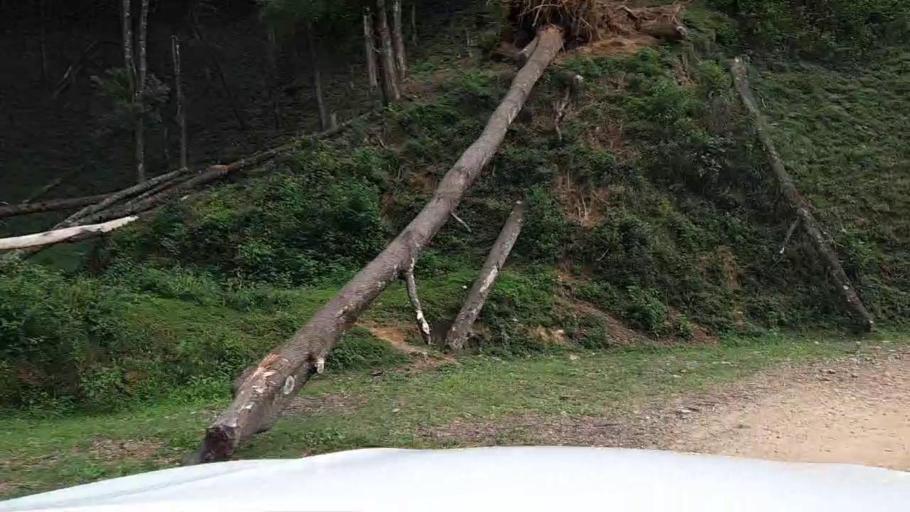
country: RW
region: Western Province
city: Kibuye
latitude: -2.2919
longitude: 29.3691
